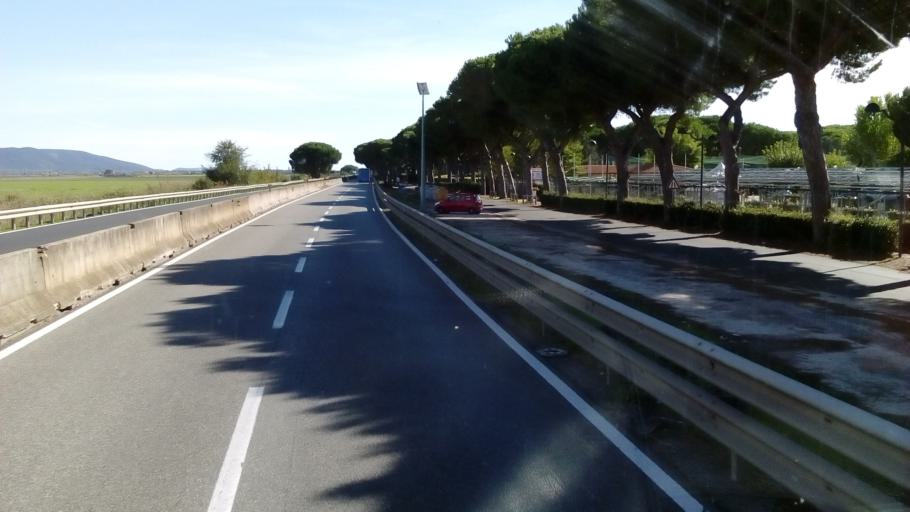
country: IT
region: Tuscany
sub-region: Provincia di Grosseto
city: Fonteblanda
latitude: 42.5348
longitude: 11.1850
